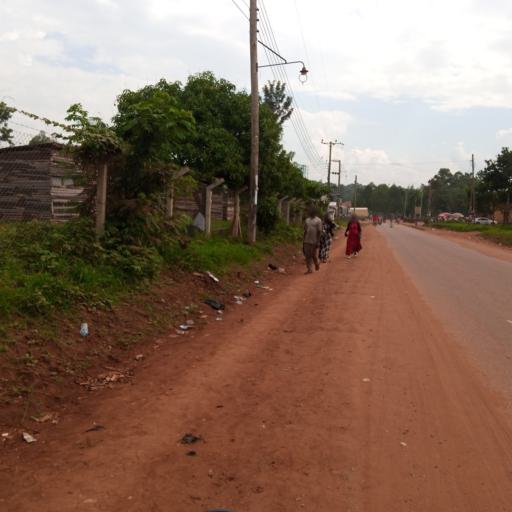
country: UG
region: Eastern Region
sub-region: Mbale District
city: Mbale
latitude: 1.0854
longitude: 34.1800
